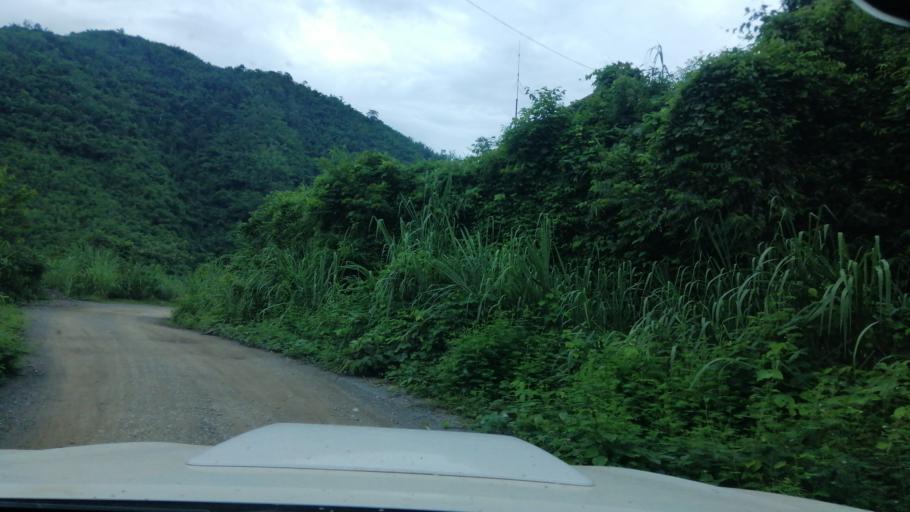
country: LA
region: Xiagnabouli
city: Sainyabuli
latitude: 19.1848
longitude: 101.7989
